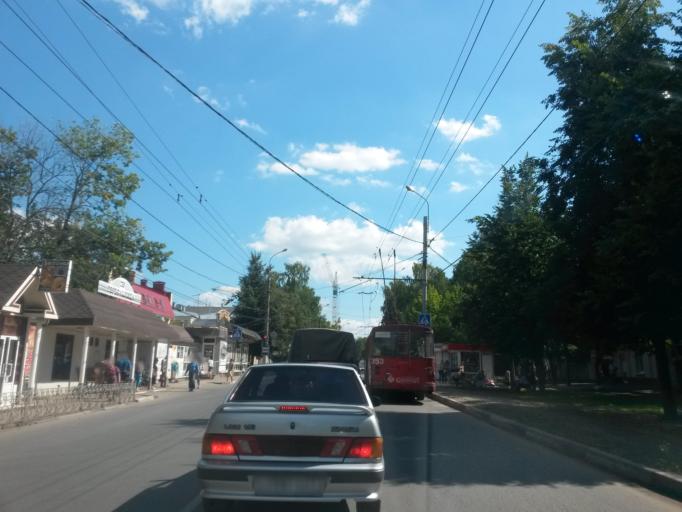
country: RU
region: Ivanovo
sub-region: Gorod Ivanovo
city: Ivanovo
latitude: 56.9858
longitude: 40.9914
